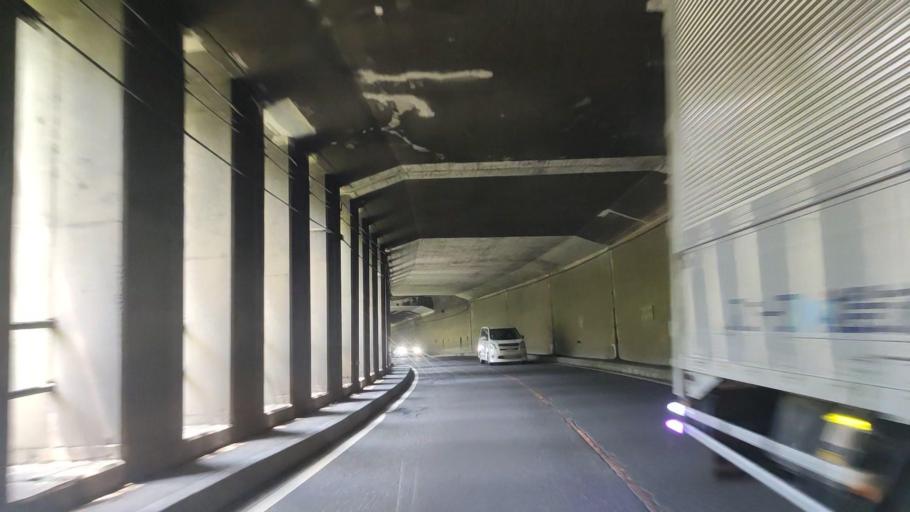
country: JP
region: Niigata
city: Itoigawa
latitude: 36.9159
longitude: 137.8722
